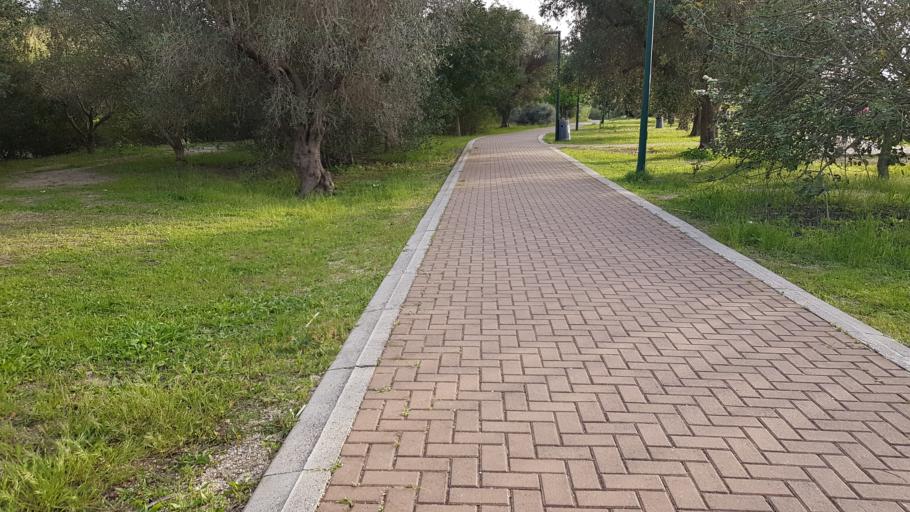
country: IT
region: Apulia
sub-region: Provincia di Brindisi
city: Brindisi
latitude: 40.6386
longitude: 17.9217
